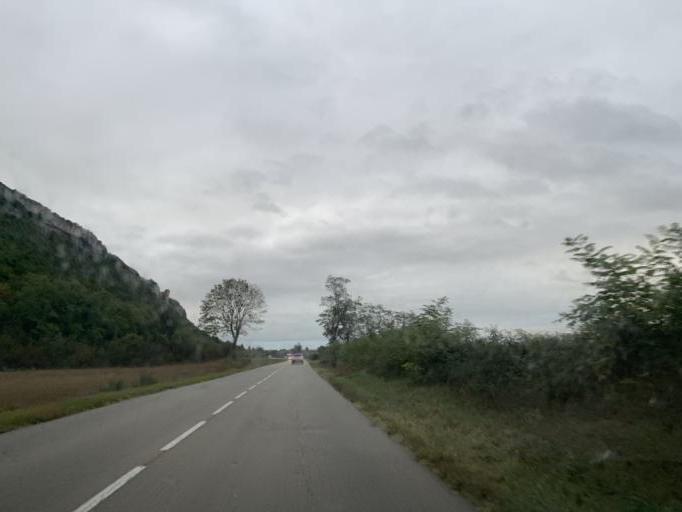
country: FR
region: Rhone-Alpes
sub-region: Departement de l'Ain
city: Villebois
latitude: 45.8186
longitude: 5.4487
